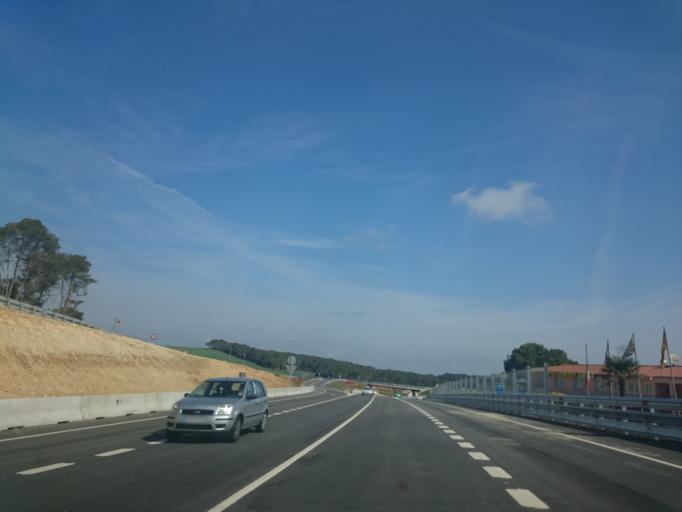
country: ES
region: Catalonia
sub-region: Provincia de Girona
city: Cervia de Ter
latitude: 42.0945
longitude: 2.8926
